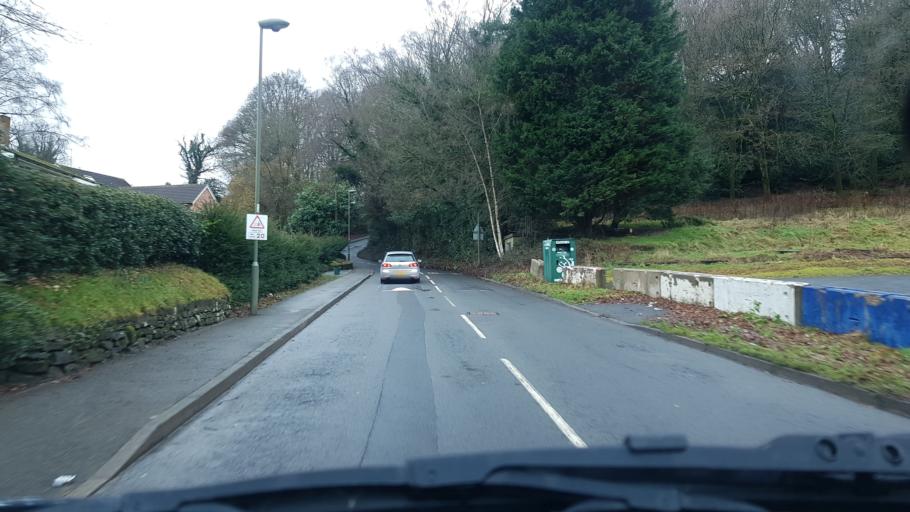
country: GB
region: England
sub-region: Surrey
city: Hindhead
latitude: 51.0899
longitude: -0.7439
